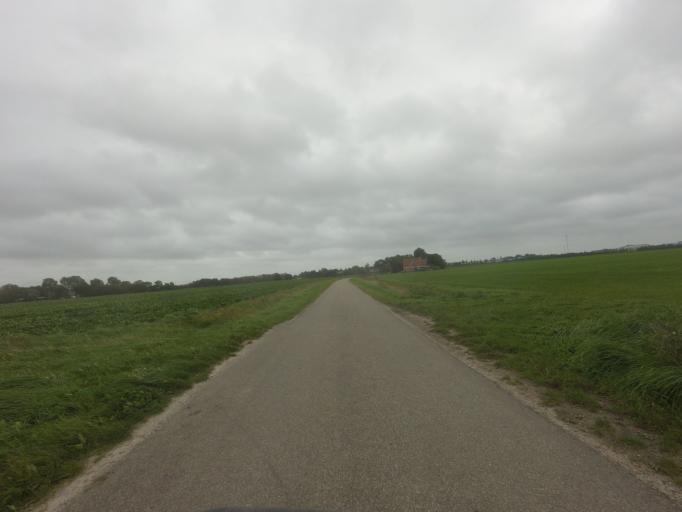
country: NL
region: Friesland
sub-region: Gemeente Leeuwarderadeel
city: Stiens
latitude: 53.2727
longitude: 5.7517
